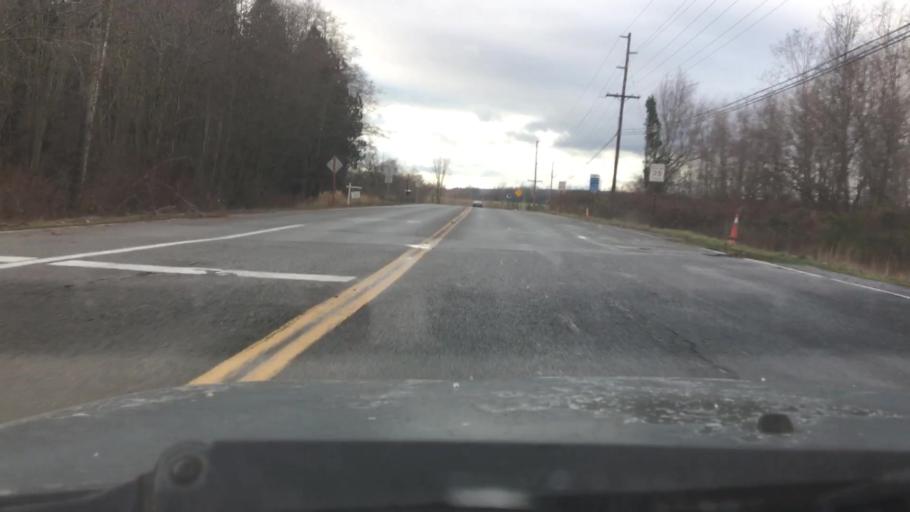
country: US
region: Washington
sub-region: Whatcom County
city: Marietta-Alderwood
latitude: 48.8179
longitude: -122.5658
